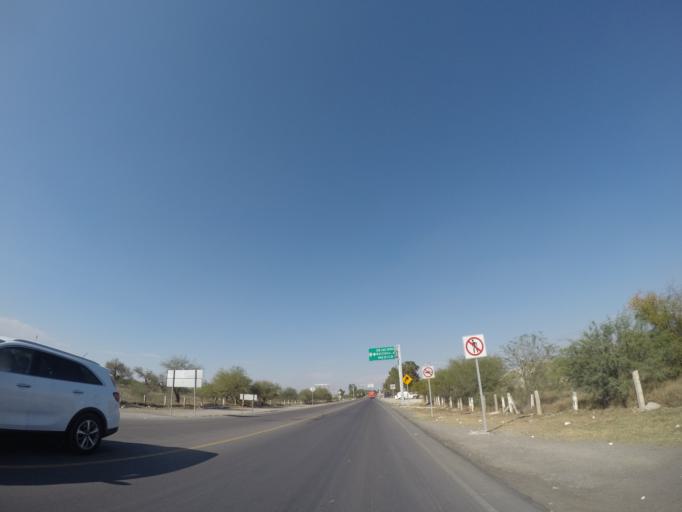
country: MX
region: San Luis Potosi
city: Rio Verde
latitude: 21.9225
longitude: -99.9596
